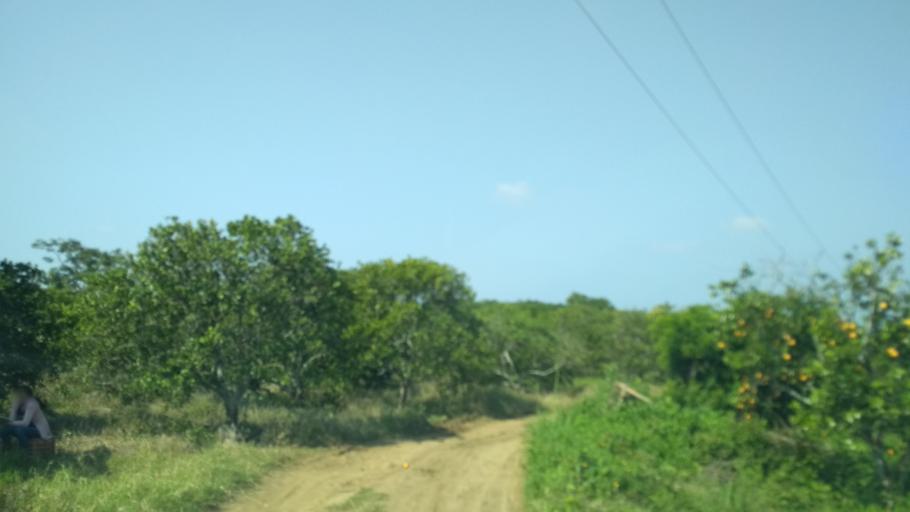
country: MX
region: Puebla
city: San Jose Acateno
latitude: 20.2041
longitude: -97.1815
